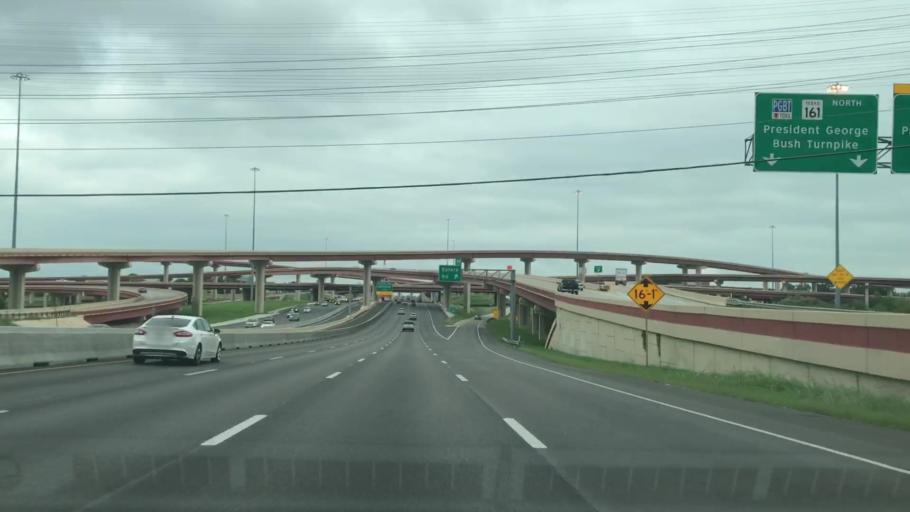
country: US
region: Texas
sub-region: Tarrant County
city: Euless
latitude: 32.8368
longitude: -97.0215
